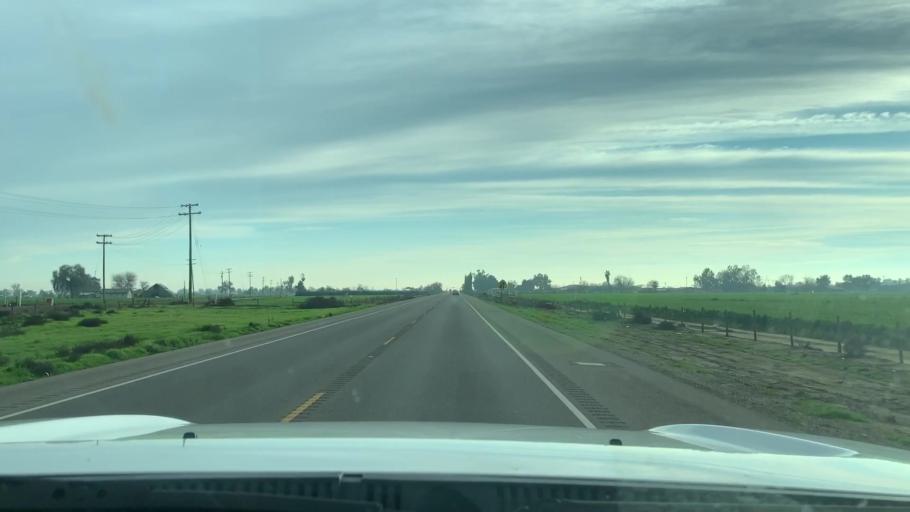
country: US
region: California
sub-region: Fresno County
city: Riverdale
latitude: 36.4429
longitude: -119.7988
